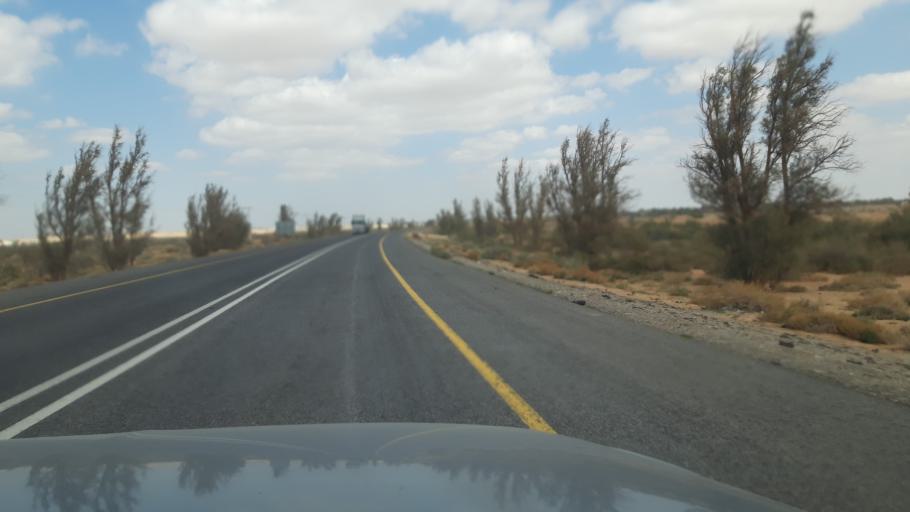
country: JO
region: Amman
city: Al Azraq ash Shamali
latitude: 31.8100
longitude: 36.7984
